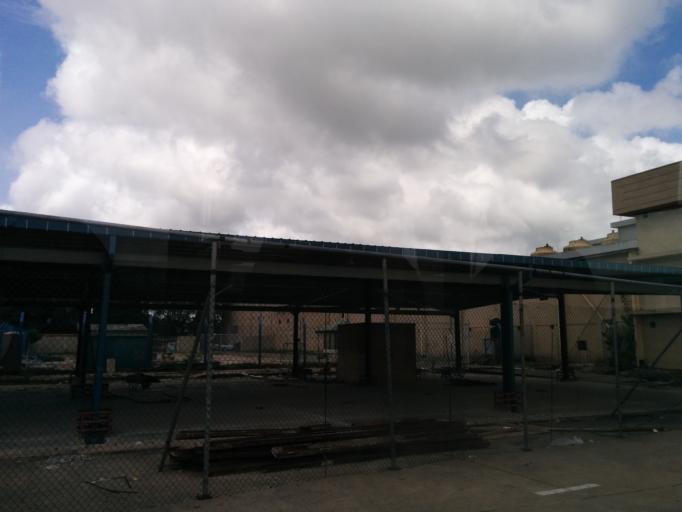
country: LK
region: Western
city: Katunayaka
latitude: 7.1763
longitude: 79.8870
